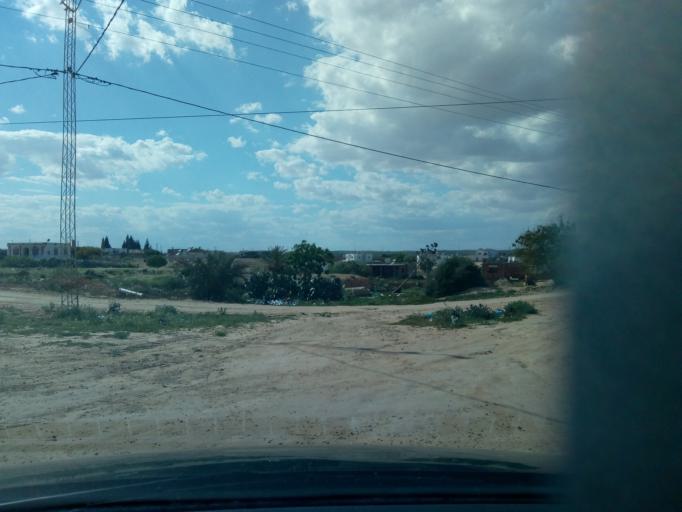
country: TN
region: Safaqis
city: Sfax
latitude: 34.7278
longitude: 10.6054
